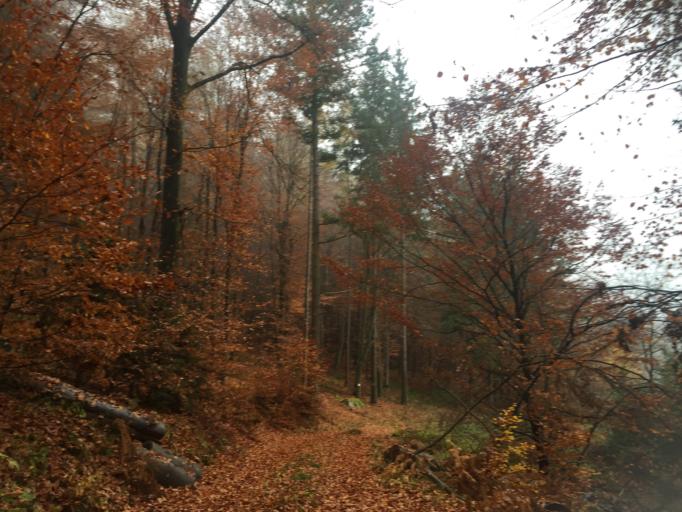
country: DE
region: Hesse
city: Hirschhorn
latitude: 49.4424
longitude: 8.8836
